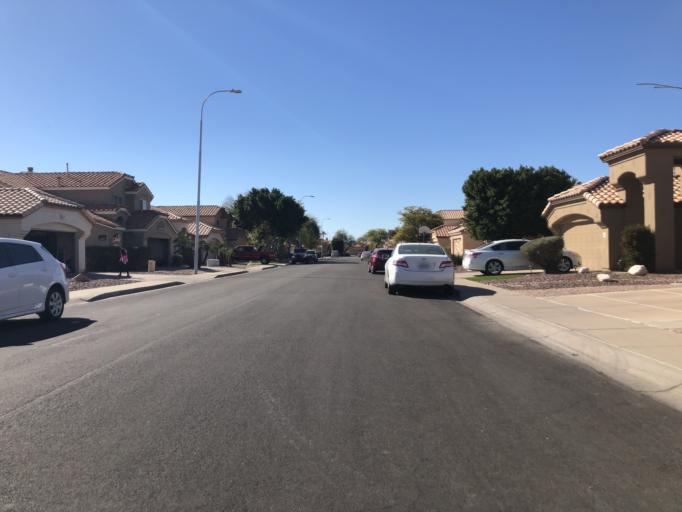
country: US
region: Arizona
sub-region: Maricopa County
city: Guadalupe
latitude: 33.3123
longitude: -111.9251
